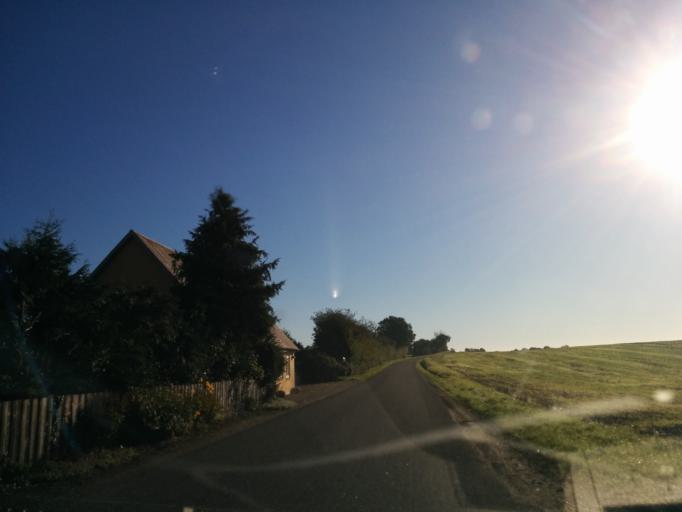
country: DK
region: South Denmark
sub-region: Kolding Kommune
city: Sonder Bjert
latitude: 55.4045
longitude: 9.5513
